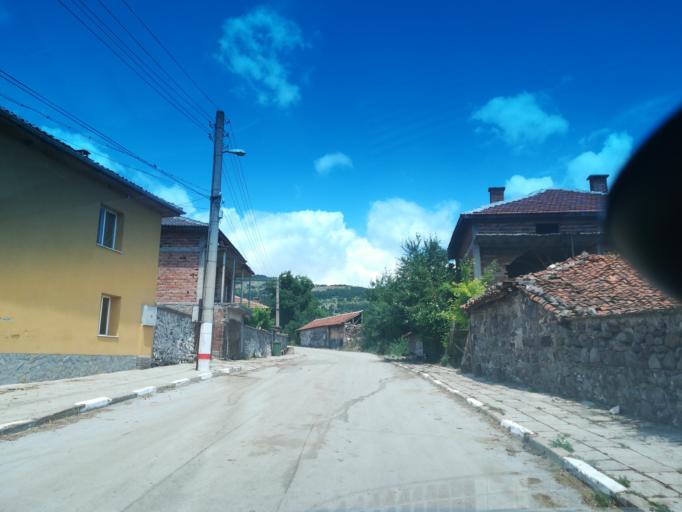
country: BG
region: Khaskovo
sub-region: Obshtina Mineralni Bani
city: Mineralni Bani
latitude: 41.9481
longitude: 25.2470
